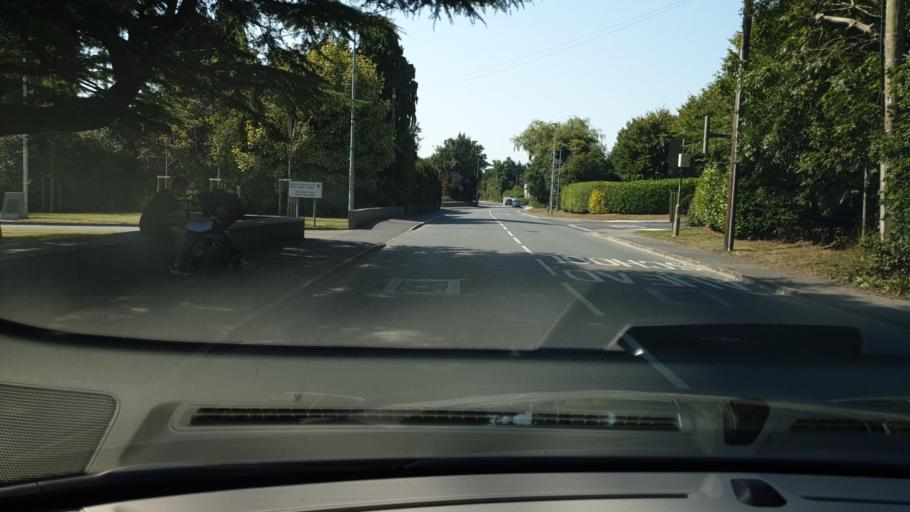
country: IE
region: Leinster
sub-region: An Mhi
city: Dunshaughlin
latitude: 53.5147
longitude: -6.5443
